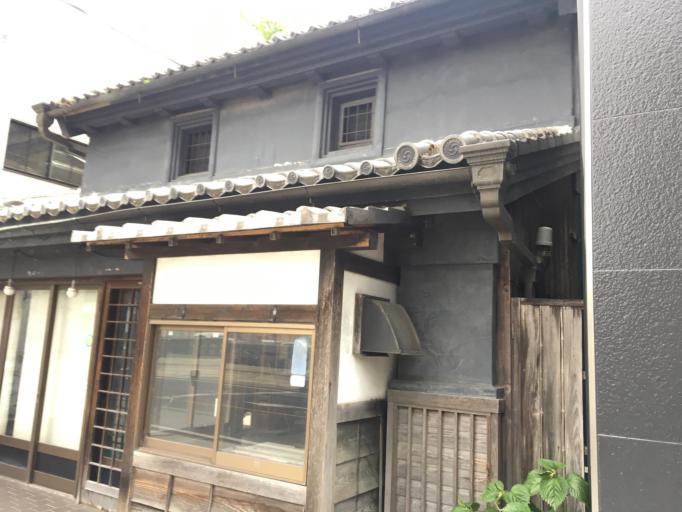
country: JP
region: Tochigi
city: Tochigi
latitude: 36.3789
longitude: 139.7334
